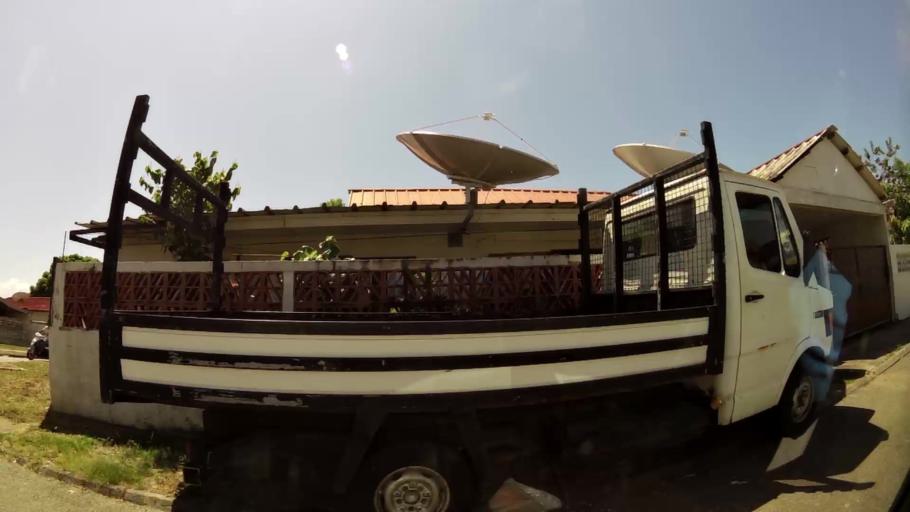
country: GF
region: Guyane
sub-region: Guyane
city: Kourou
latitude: 5.1685
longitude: -52.6535
